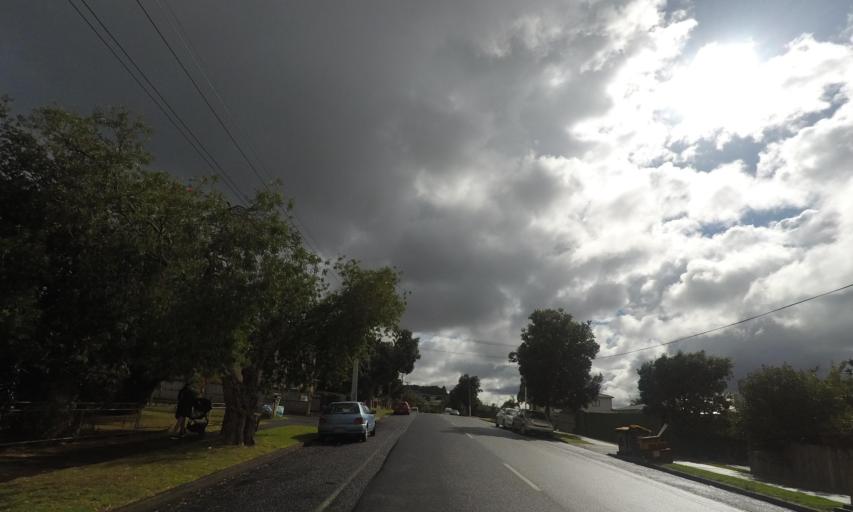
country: NZ
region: Auckland
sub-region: Auckland
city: Mangere
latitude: -36.9527
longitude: 174.7862
